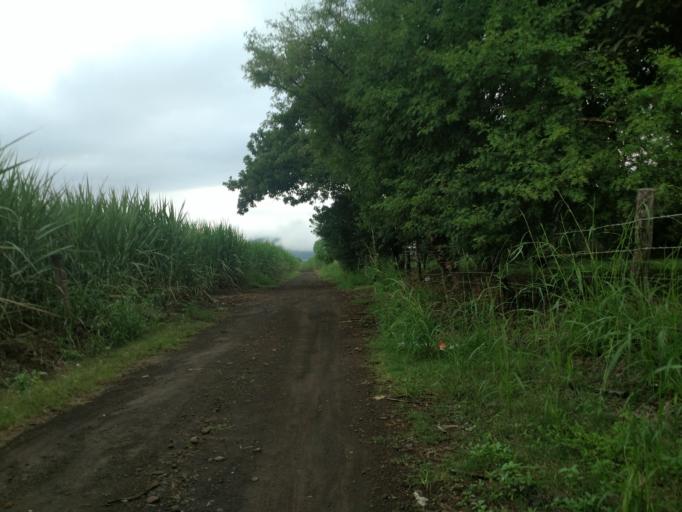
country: MX
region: Nayarit
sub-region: Tepic
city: La Corregidora
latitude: 21.4705
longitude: -104.8022
